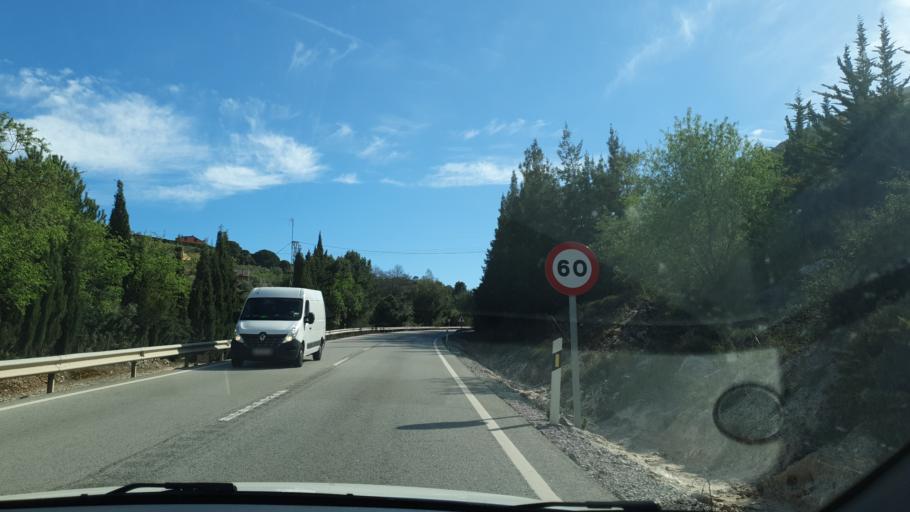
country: ES
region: Andalusia
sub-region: Provincia de Malaga
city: Ojen
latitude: 36.5886
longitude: -4.8520
